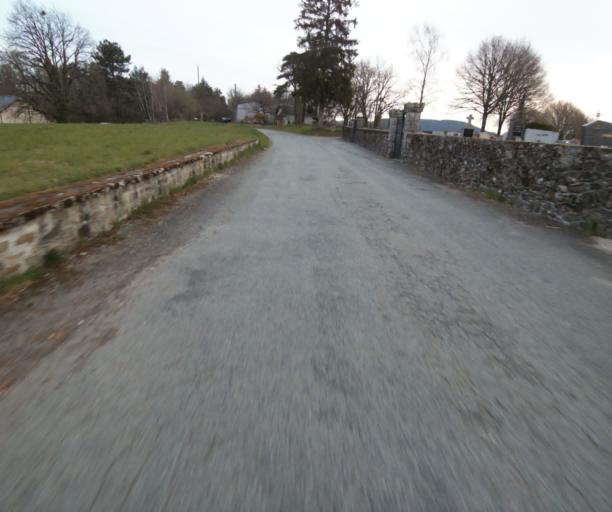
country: FR
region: Limousin
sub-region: Departement de la Correze
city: Correze
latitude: 45.4261
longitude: 1.8363
